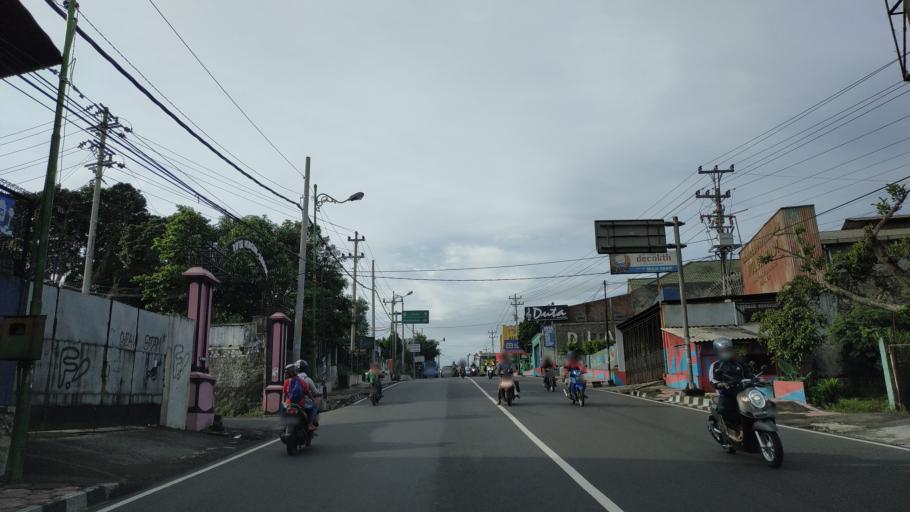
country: ID
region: Central Java
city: Salatiga
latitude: -7.3444
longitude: 110.5108
